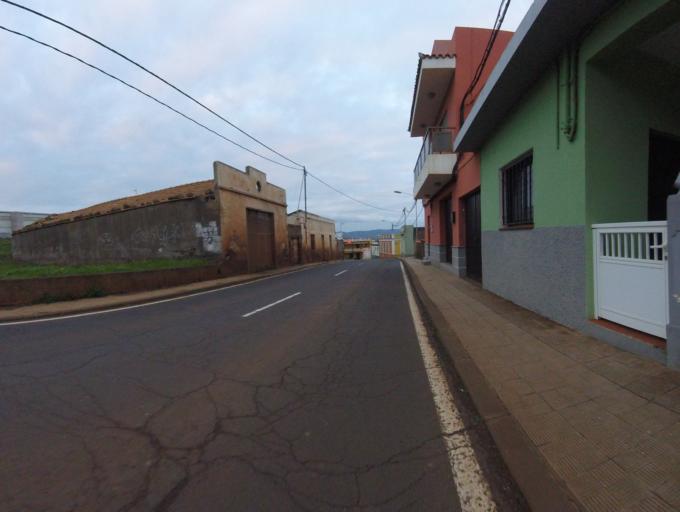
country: ES
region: Canary Islands
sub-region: Provincia de Santa Cruz de Tenerife
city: La Laguna
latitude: 28.4414
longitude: -16.3349
